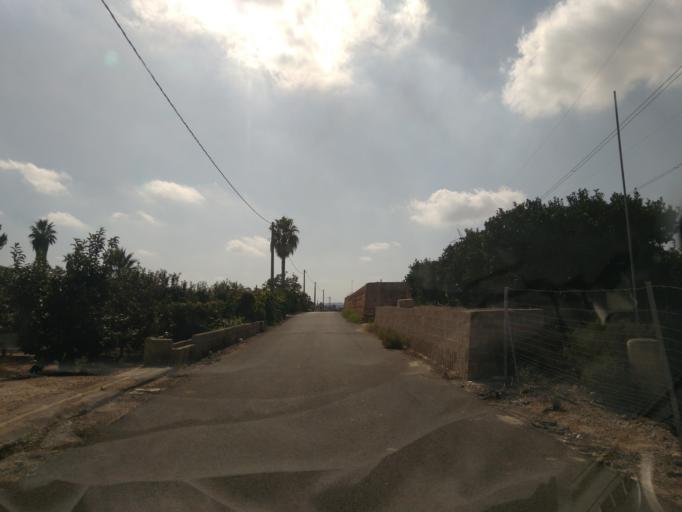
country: ES
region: Valencia
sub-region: Provincia de Valencia
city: Benimodo
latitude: 39.1787
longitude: -0.5511
